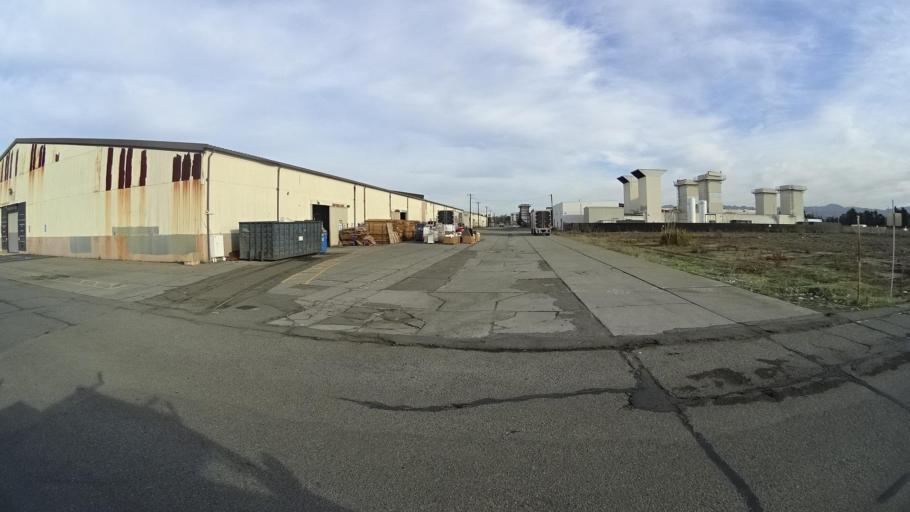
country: US
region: California
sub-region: Alameda County
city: Oakland
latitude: 37.7753
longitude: -122.2951
